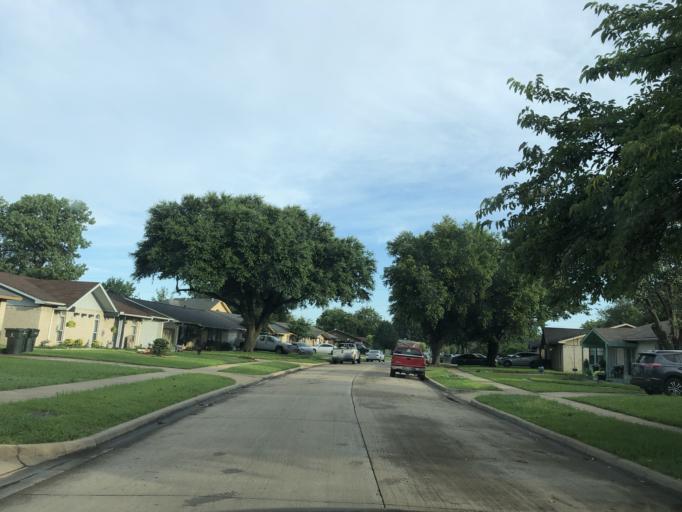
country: US
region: Texas
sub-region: Dallas County
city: Rowlett
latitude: 32.8514
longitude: -96.6043
